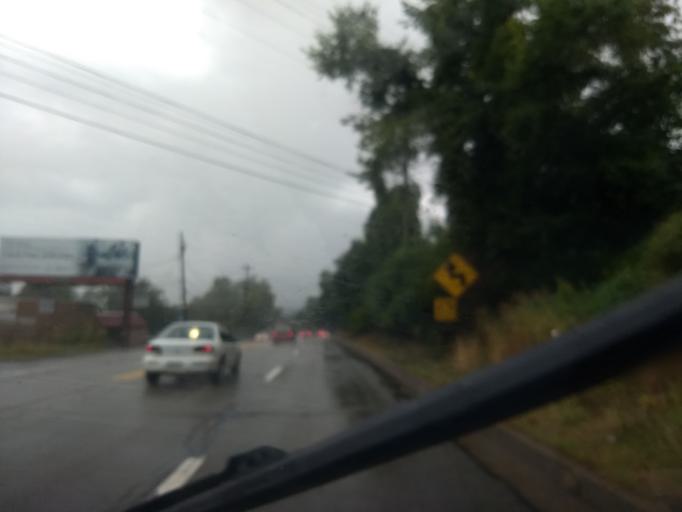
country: US
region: Pennsylvania
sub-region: Allegheny County
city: North Versailles
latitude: 40.3815
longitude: -79.8175
